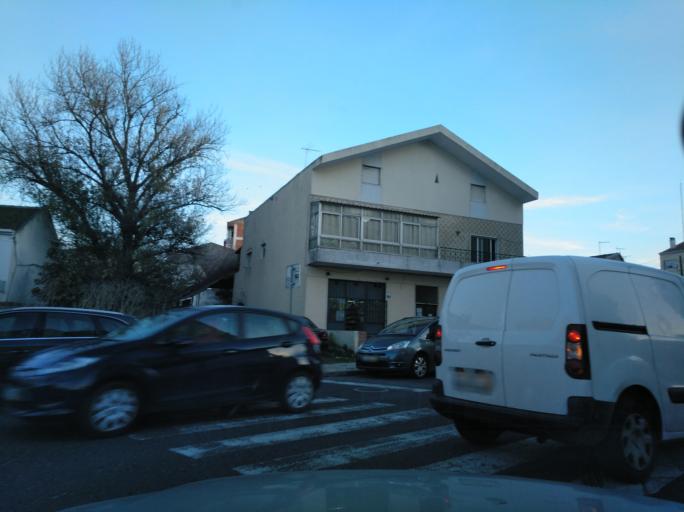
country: PT
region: Lisbon
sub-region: Odivelas
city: Olival do Basto
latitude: 38.7933
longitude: -9.1521
